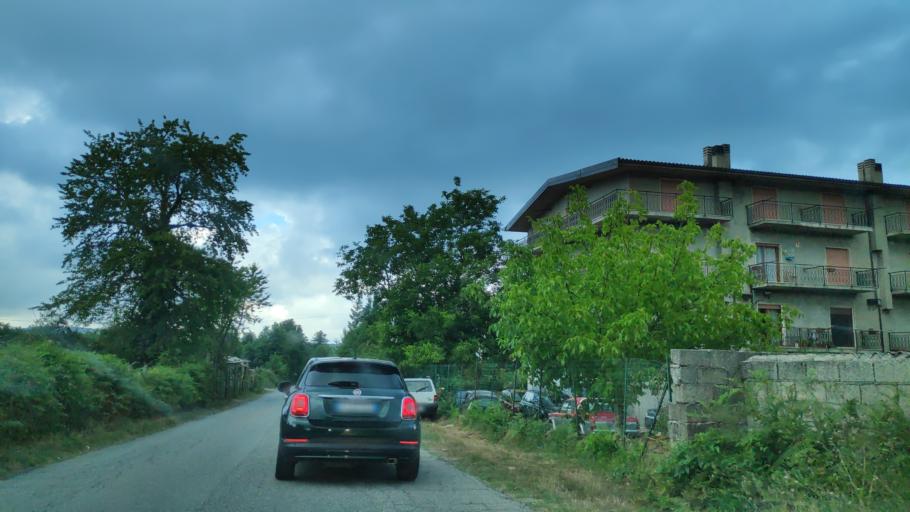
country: IT
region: Calabria
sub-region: Provincia di Vibo-Valentia
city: Serra San Bruno
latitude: 38.5577
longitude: 16.3265
